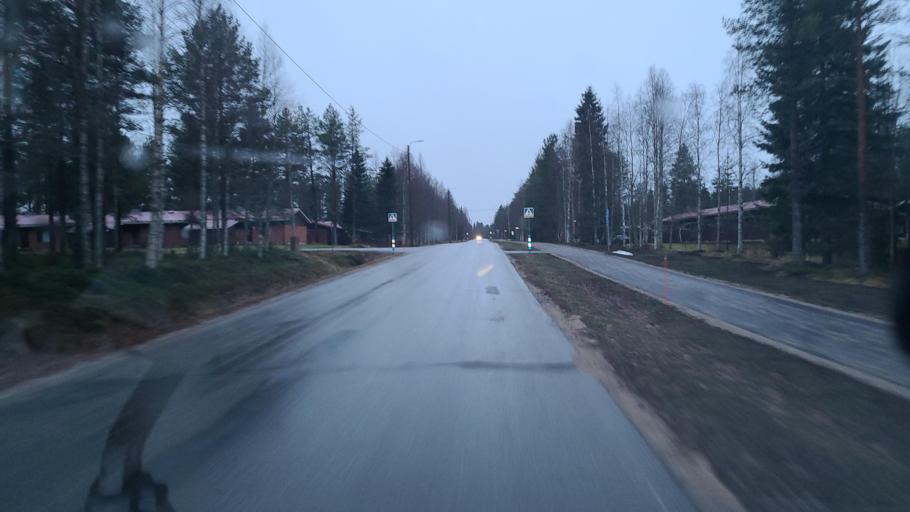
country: FI
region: Lapland
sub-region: Rovaniemi
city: Ranua
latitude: 65.9297
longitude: 26.4959
